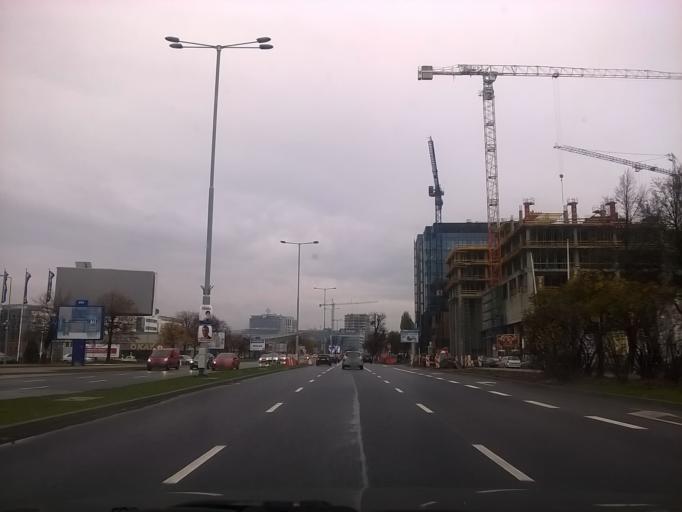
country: PL
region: Pomeranian Voivodeship
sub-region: Sopot
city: Sopot
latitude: 54.3973
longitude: 18.5776
